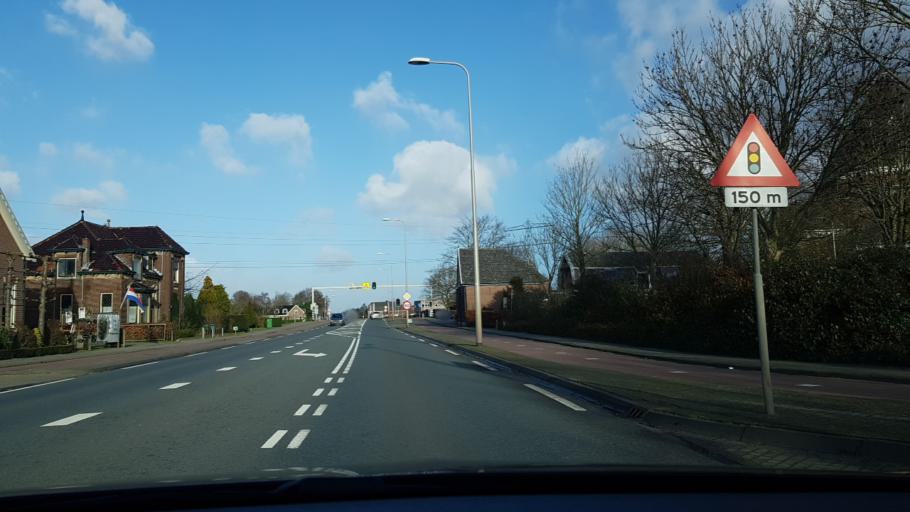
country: NL
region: South Holland
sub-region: Gemeente Teylingen
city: Sassenheim
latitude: 52.2351
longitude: 4.5331
